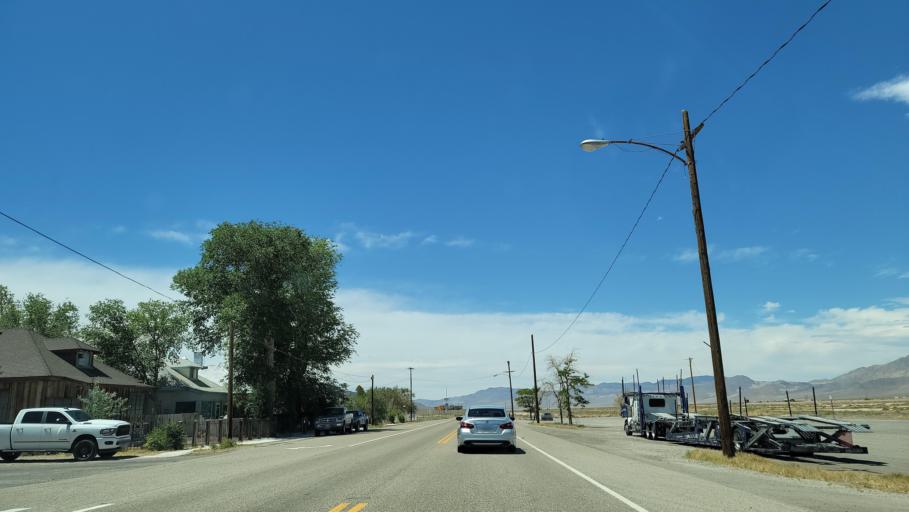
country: US
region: Nevada
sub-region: Mineral County
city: Hawthorne
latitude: 38.3932
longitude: -118.1104
